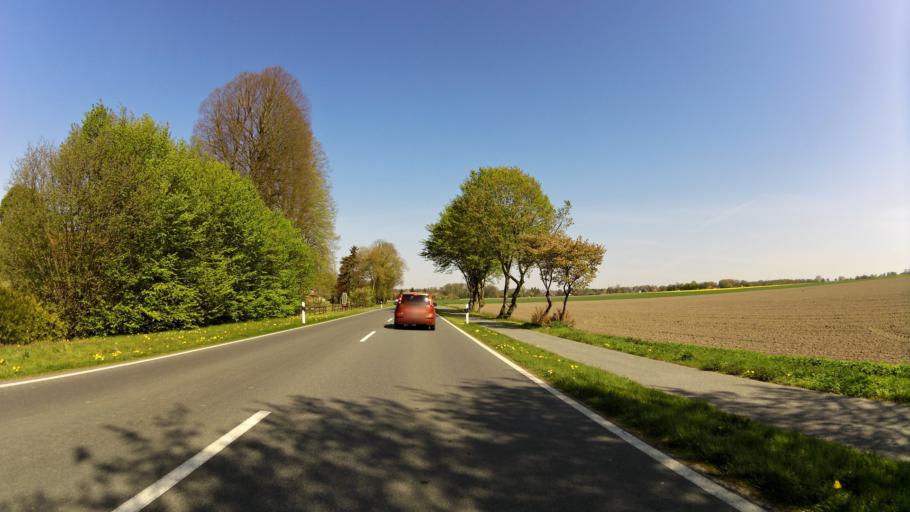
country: DE
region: Lower Saxony
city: Ganderkesee
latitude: 53.0779
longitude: 8.5261
